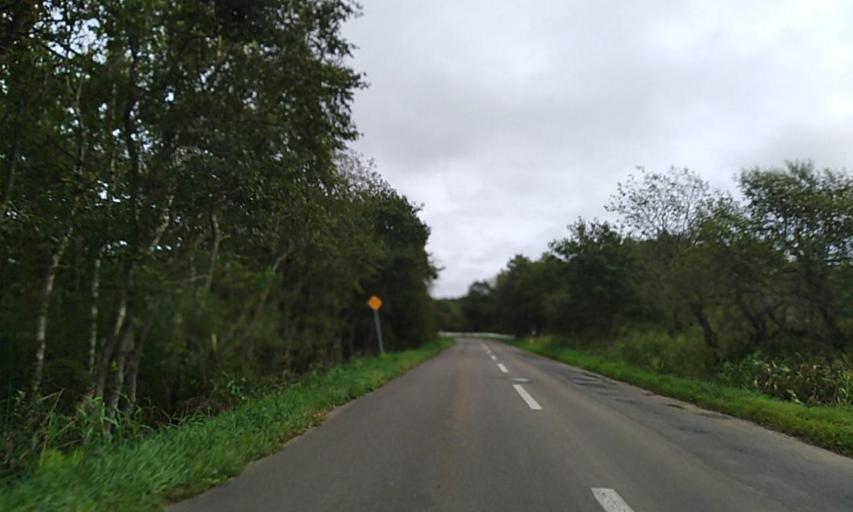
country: JP
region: Hokkaido
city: Nemuro
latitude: 43.2617
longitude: 145.2609
